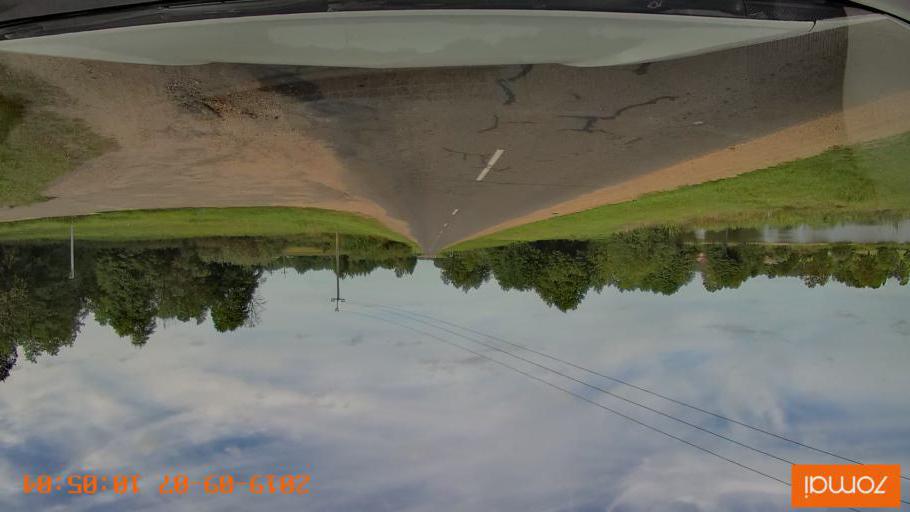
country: BY
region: Grodnenskaya
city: Voranava
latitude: 54.0427
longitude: 25.4092
